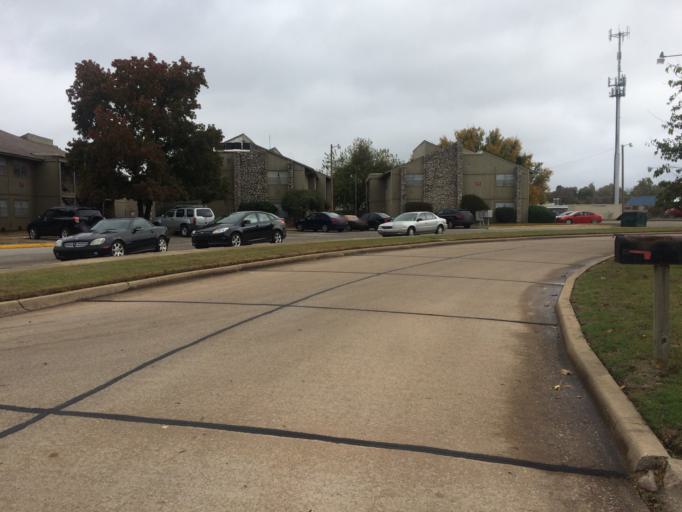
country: US
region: Oklahoma
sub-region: Cleveland County
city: Norman
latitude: 35.2021
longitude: -97.4629
